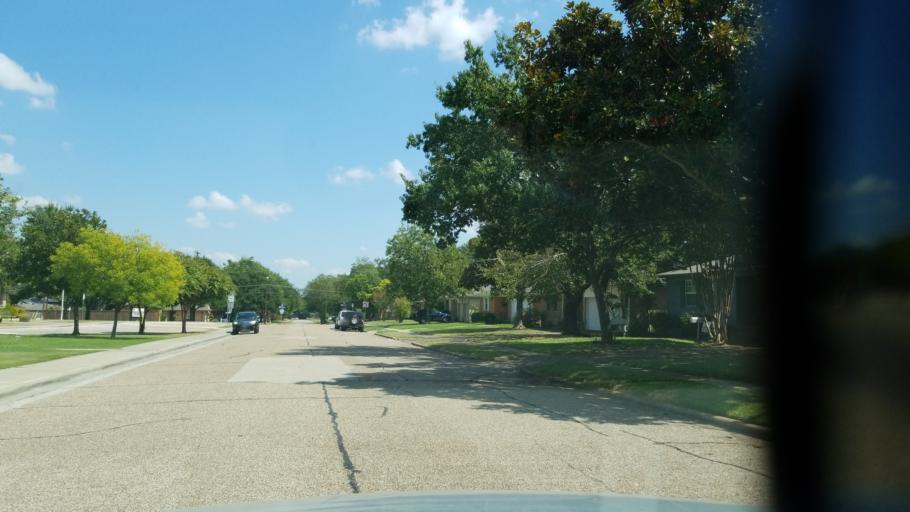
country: US
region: Texas
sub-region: Dallas County
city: Richardson
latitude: 32.9608
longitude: -96.7637
